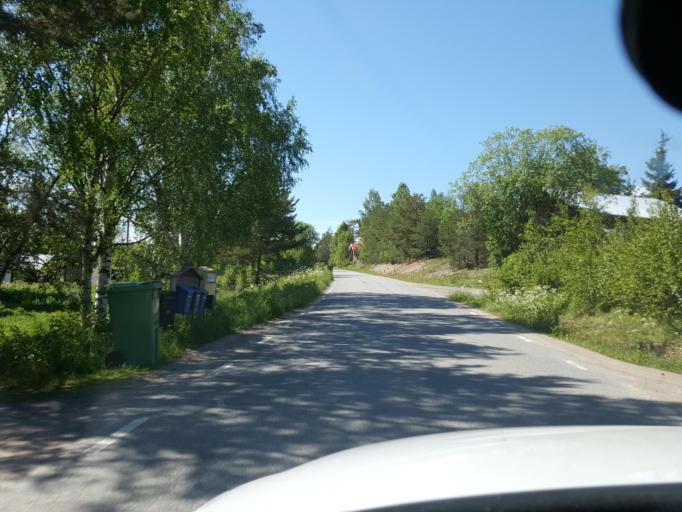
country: SE
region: Gaevleborg
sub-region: Ljusdals Kommun
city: Jaervsoe
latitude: 61.7470
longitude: 16.2652
